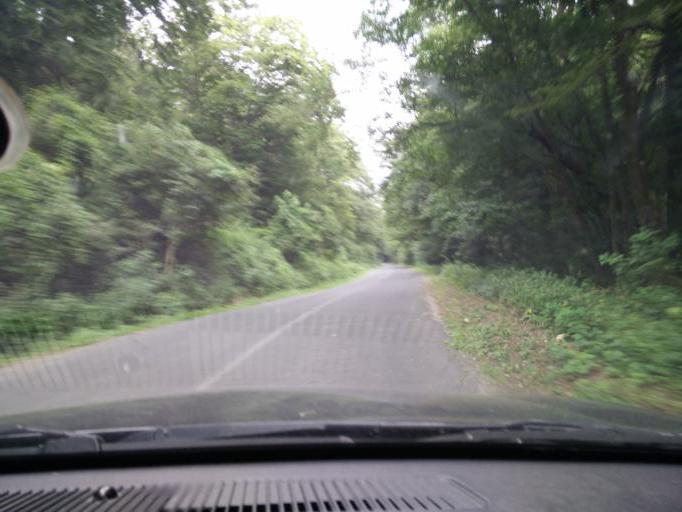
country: HU
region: Komarom-Esztergom
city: Tardos
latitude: 47.6777
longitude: 18.4361
